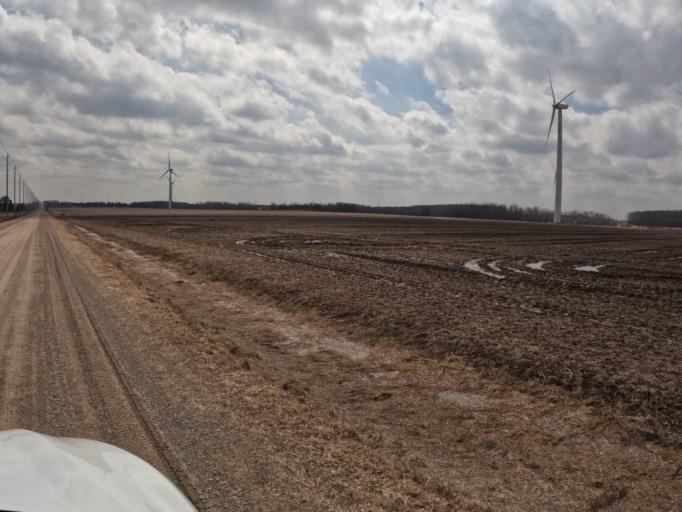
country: CA
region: Ontario
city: Shelburne
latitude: 44.0410
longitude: -80.3176
